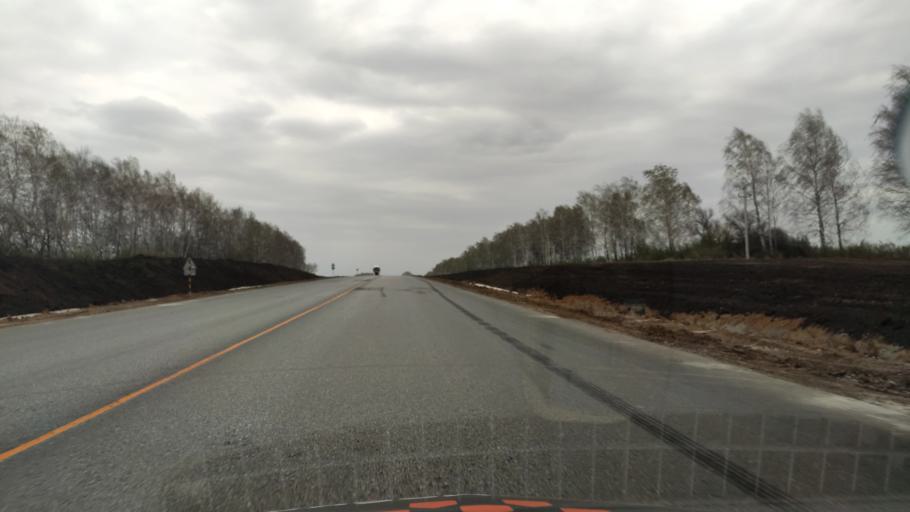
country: RU
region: Kursk
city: Gorshechnoye
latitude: 51.5482
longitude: 38.1052
